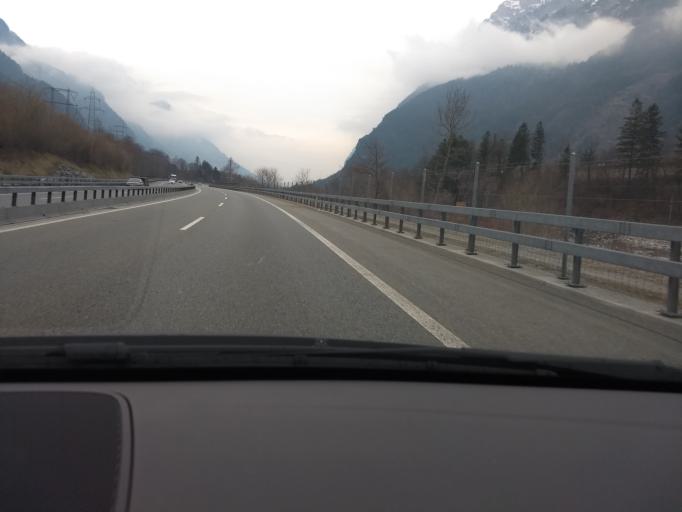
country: CH
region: Uri
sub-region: Uri
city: Silenen
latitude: 46.8001
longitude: 8.6633
